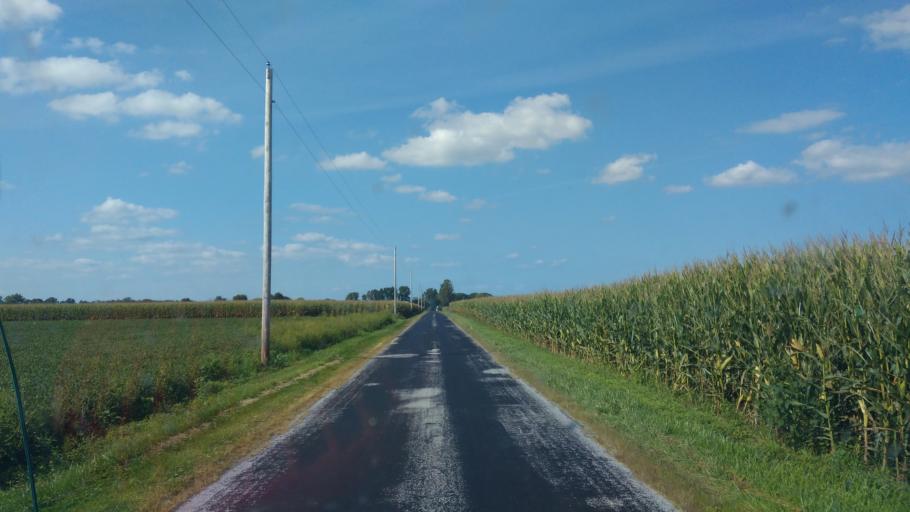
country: US
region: Ohio
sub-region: Hardin County
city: Forest
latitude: 40.7042
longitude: -83.4780
